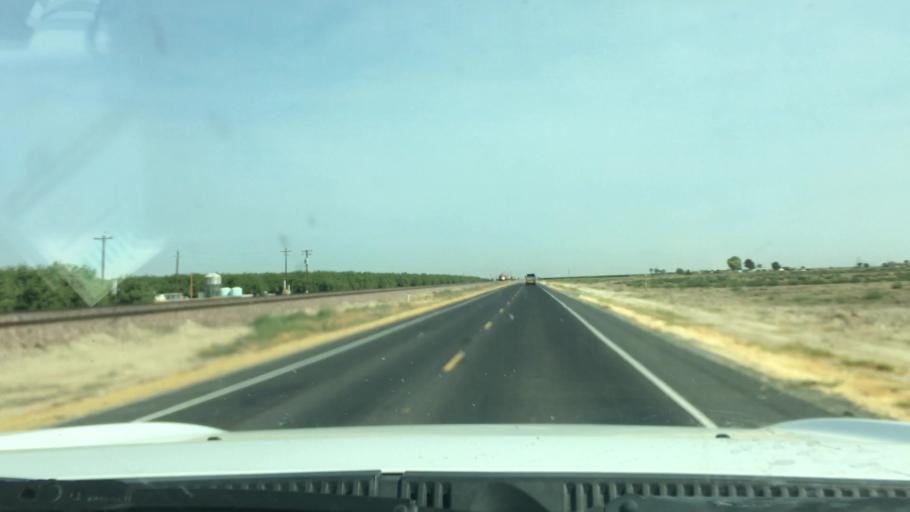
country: US
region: California
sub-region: Kern County
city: Delano
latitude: 35.7669
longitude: -119.3471
